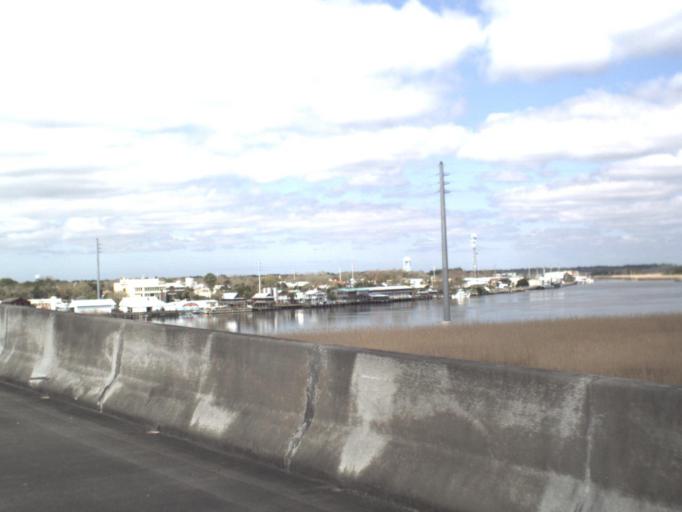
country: US
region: Florida
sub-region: Franklin County
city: Apalachicola
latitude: 29.7250
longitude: -84.9757
